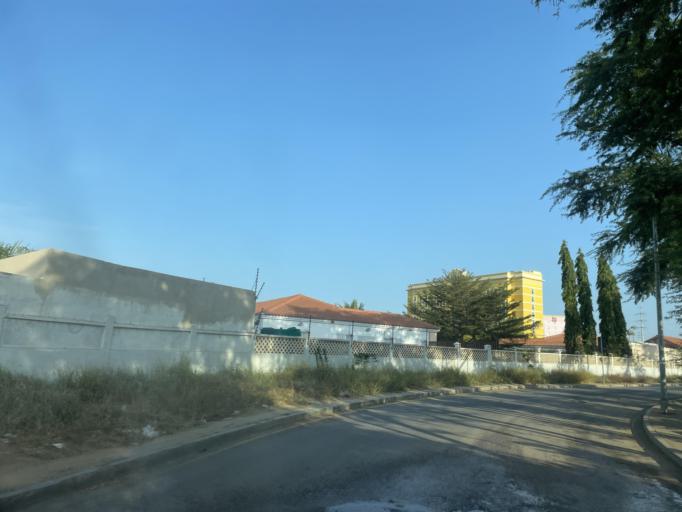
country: AO
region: Luanda
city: Luanda
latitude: -8.9115
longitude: 13.1901
